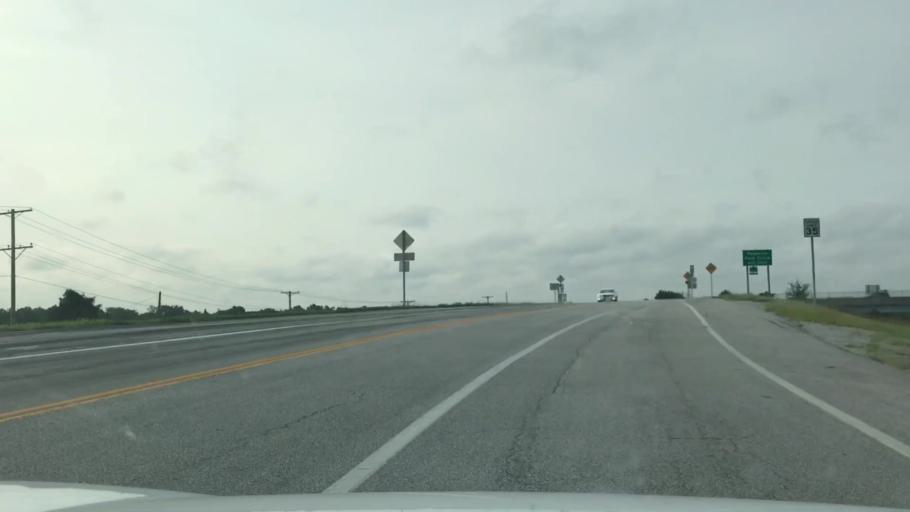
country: US
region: Missouri
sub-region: Saint Charles County
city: Weldon Spring
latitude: 38.7046
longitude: -90.6734
